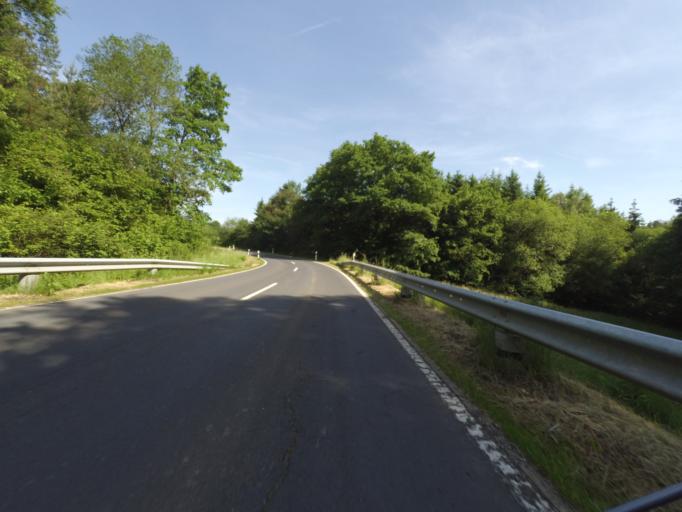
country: DE
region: Rheinland-Pfalz
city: Landkern
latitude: 50.2179
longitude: 7.1516
